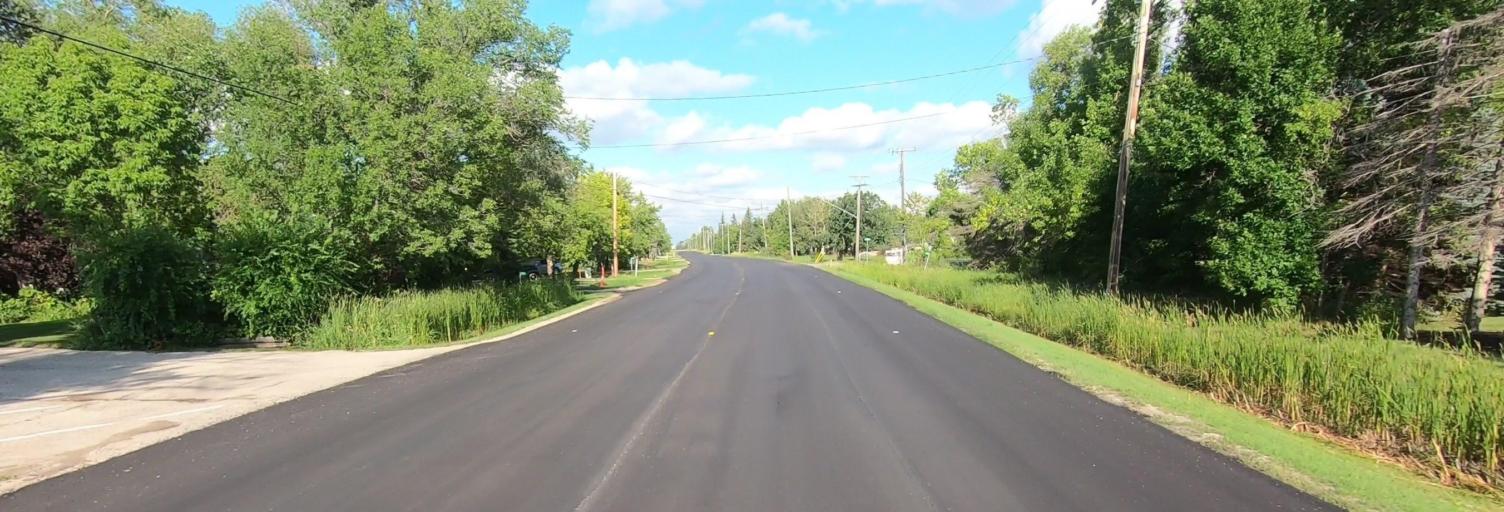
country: CA
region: Manitoba
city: Selkirk
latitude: 50.0317
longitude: -97.0048
